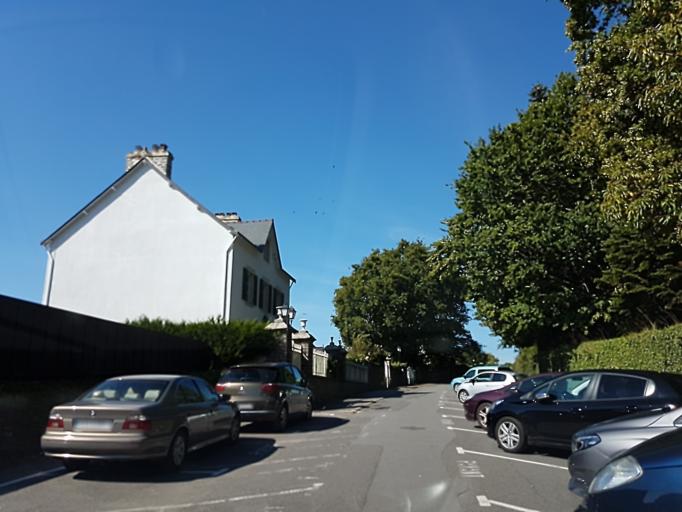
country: FR
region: Brittany
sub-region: Departement du Morbihan
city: Pluherlin
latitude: 47.6988
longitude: -2.3417
